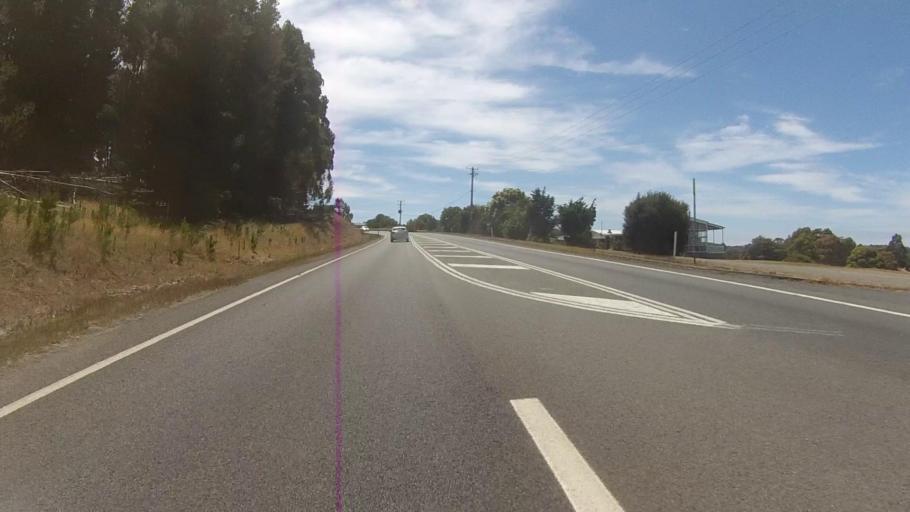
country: AU
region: Tasmania
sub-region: Kingborough
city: Margate
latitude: -43.0047
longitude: 147.2746
